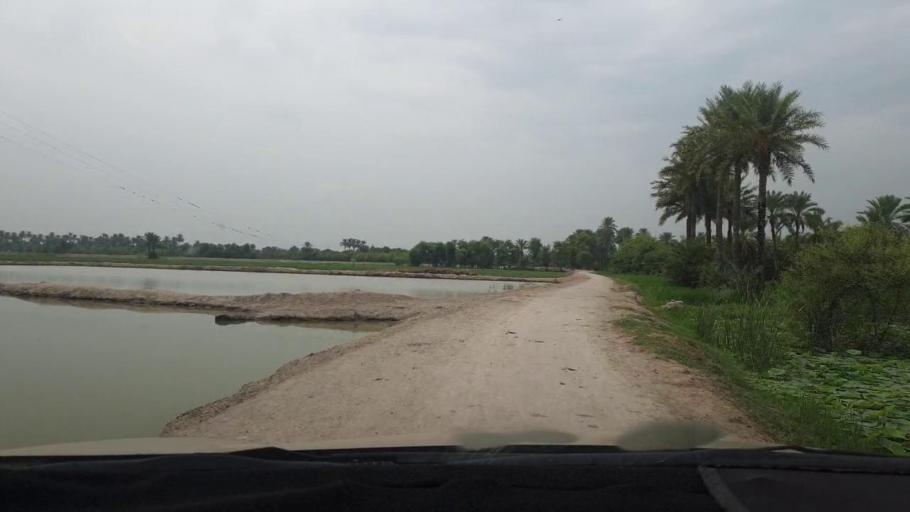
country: PK
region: Sindh
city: Larkana
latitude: 27.5742
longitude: 68.2442
